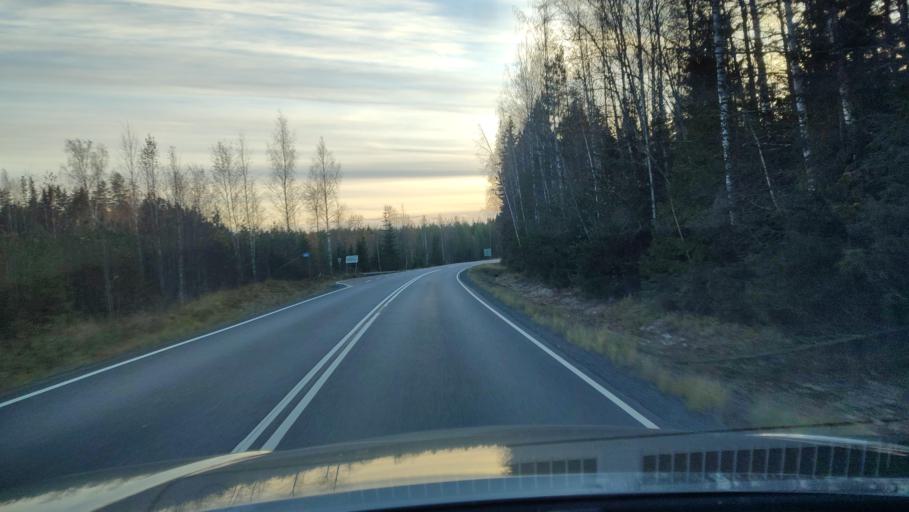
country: FI
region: Southern Ostrobothnia
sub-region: Suupohja
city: Karijoki
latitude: 62.2848
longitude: 21.6225
